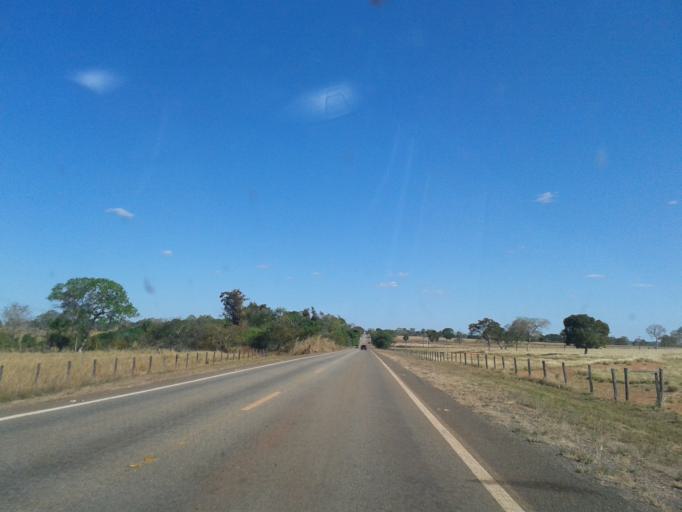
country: BR
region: Goias
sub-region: Mozarlandia
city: Mozarlandia
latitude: -14.2706
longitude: -50.3996
